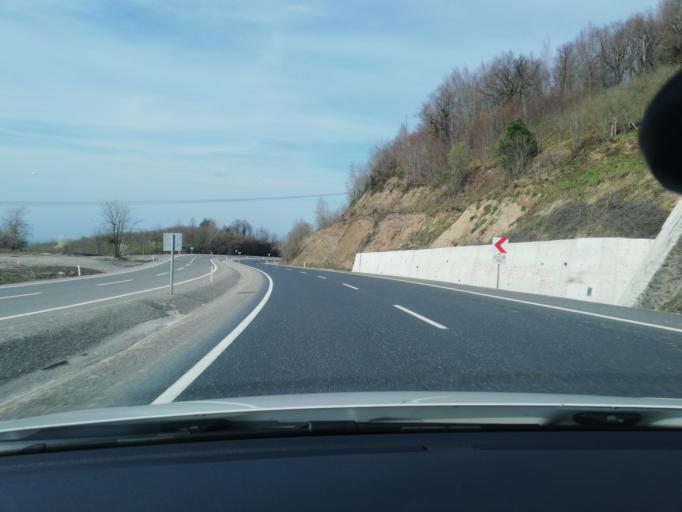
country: TR
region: Zonguldak
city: Kozlu
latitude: 41.3389
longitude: 31.6293
